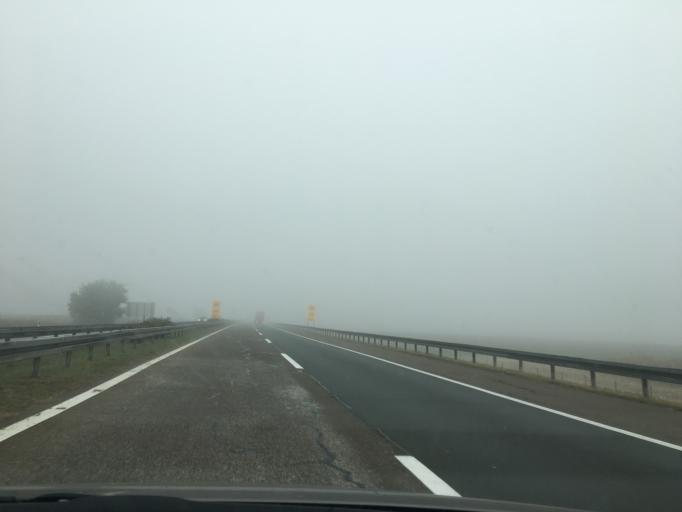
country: RS
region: Autonomna Pokrajina Vojvodina
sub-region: Sremski Okrug
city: Stara Pazova
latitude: 44.9974
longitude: 20.2068
